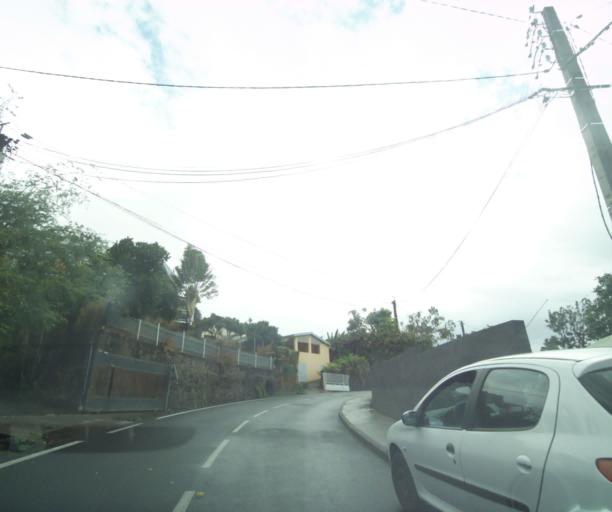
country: RE
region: Reunion
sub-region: Reunion
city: Saint-Paul
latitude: -21.0232
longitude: 55.2875
